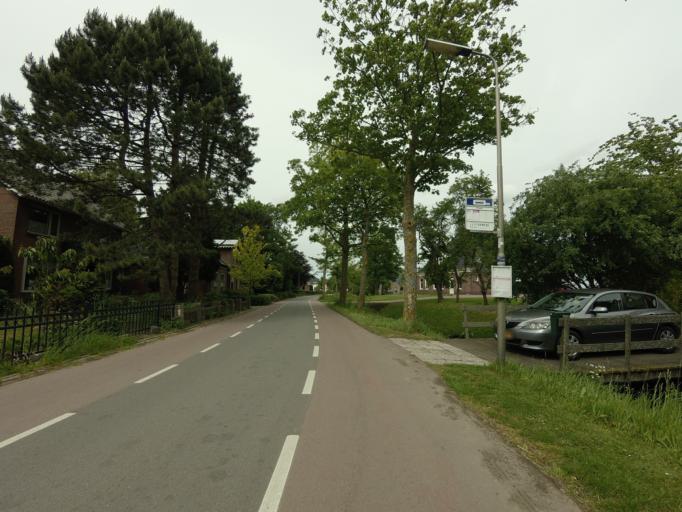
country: NL
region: North Holland
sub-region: Gemeente Hoorn
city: Hoorn
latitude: 52.6391
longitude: 5.1229
